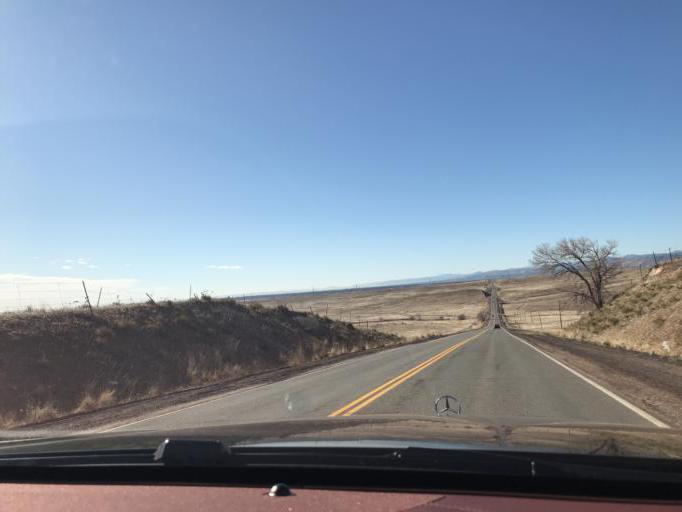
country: US
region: Colorado
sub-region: Boulder County
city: Superior
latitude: 39.9085
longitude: -105.1657
